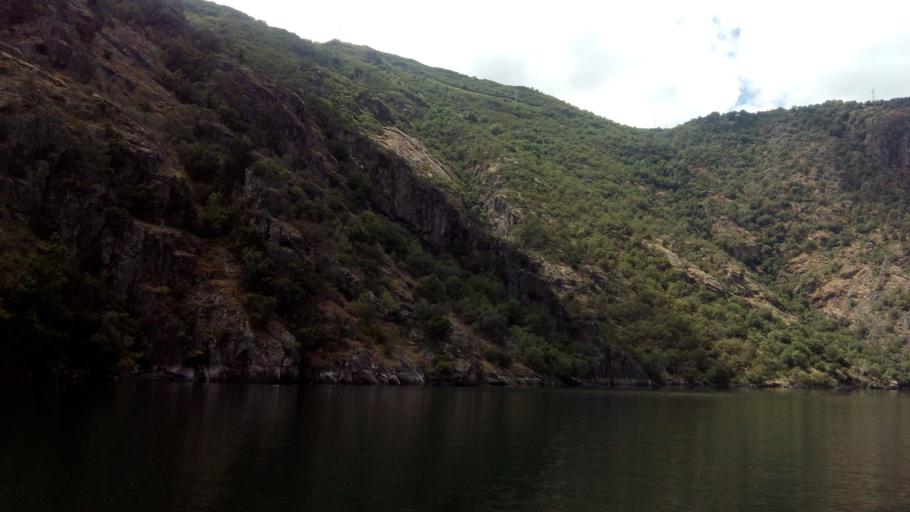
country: ES
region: Galicia
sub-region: Provincia de Lugo
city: Sober
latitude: 42.3863
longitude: -7.6098
